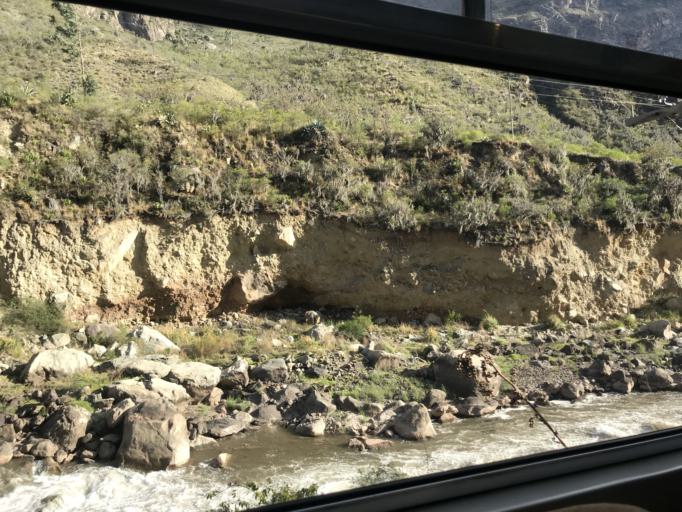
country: PE
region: Cusco
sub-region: Provincia de Urubamba
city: Ollantaytambo
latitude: -13.2241
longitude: -72.3964
